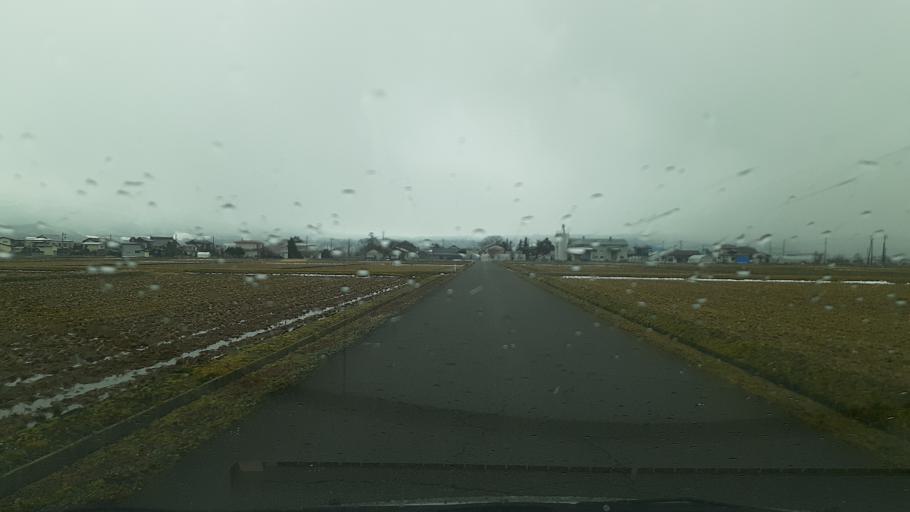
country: JP
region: Fukushima
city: Kitakata
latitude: 37.5601
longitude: 139.8798
